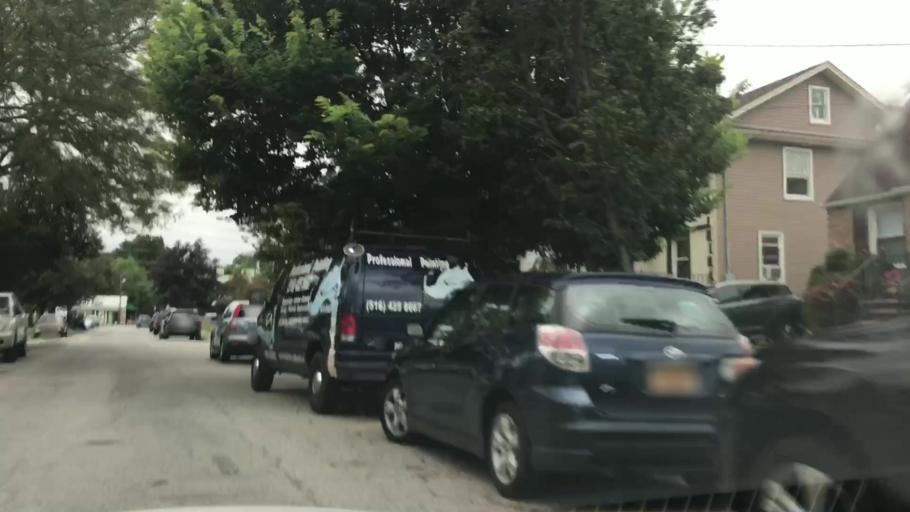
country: US
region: New York
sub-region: Nassau County
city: Hewlett
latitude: 40.6444
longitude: -73.6968
